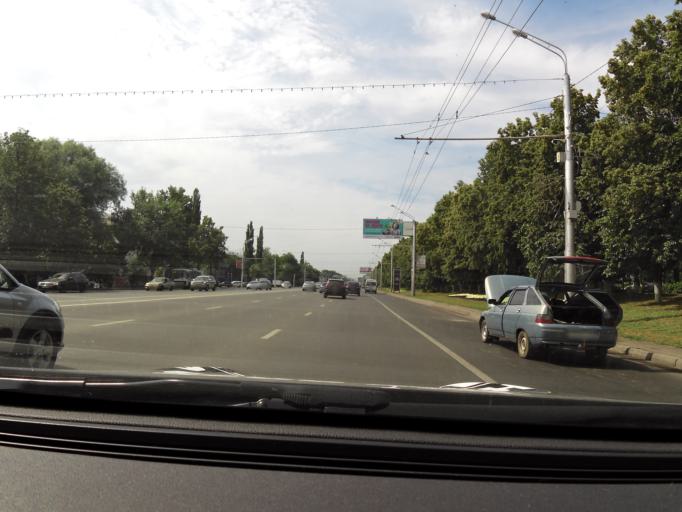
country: RU
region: Bashkortostan
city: Ufa
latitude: 54.7540
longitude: 56.0026
